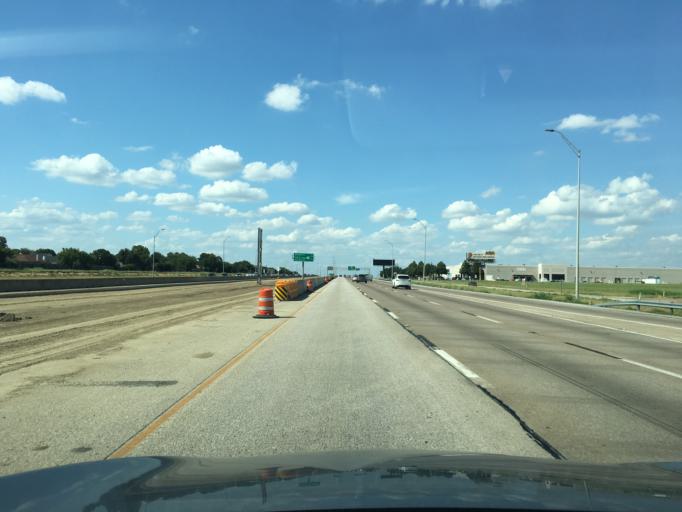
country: US
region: Texas
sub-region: Tarrant County
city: Arlington
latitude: 32.6961
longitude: -97.0625
